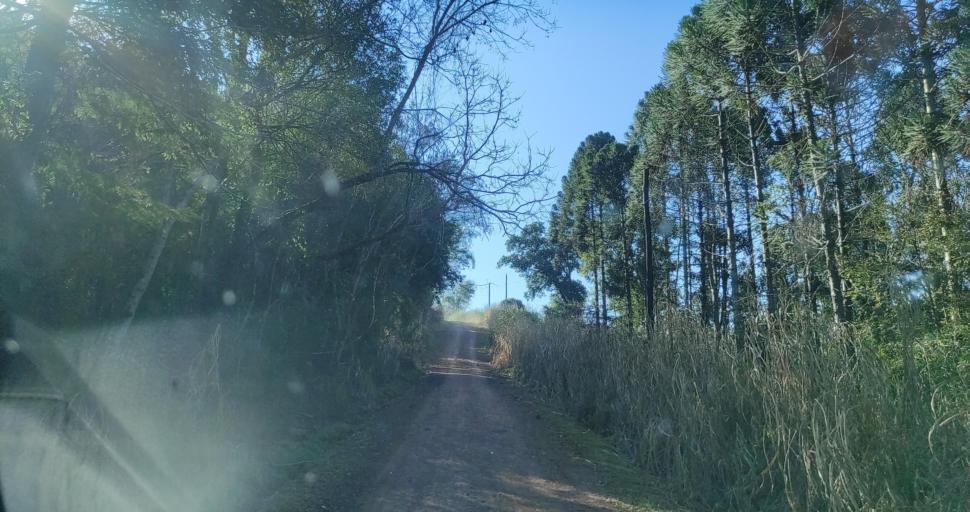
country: AR
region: Misiones
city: Capiovi
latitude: -26.8970
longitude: -55.0930
